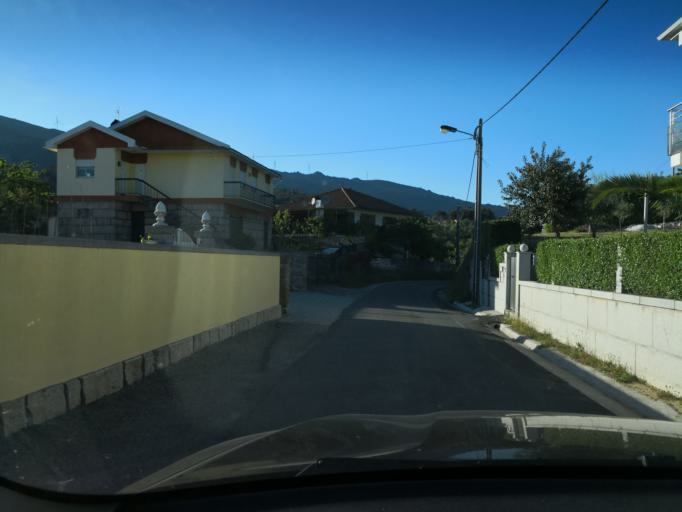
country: PT
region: Vila Real
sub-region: Vila Real
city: Vila Real
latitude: 41.3472
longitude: -7.7264
